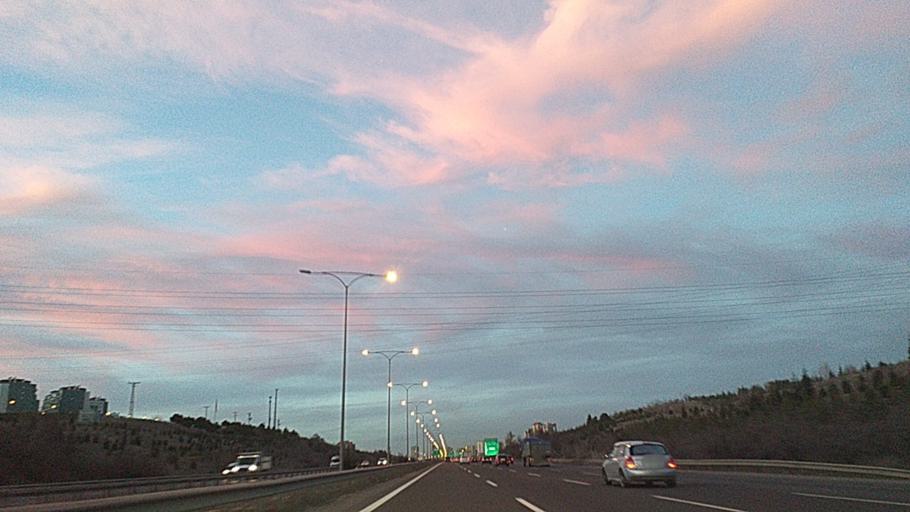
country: TR
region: Ankara
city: Etimesgut
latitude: 39.9797
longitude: 32.6359
